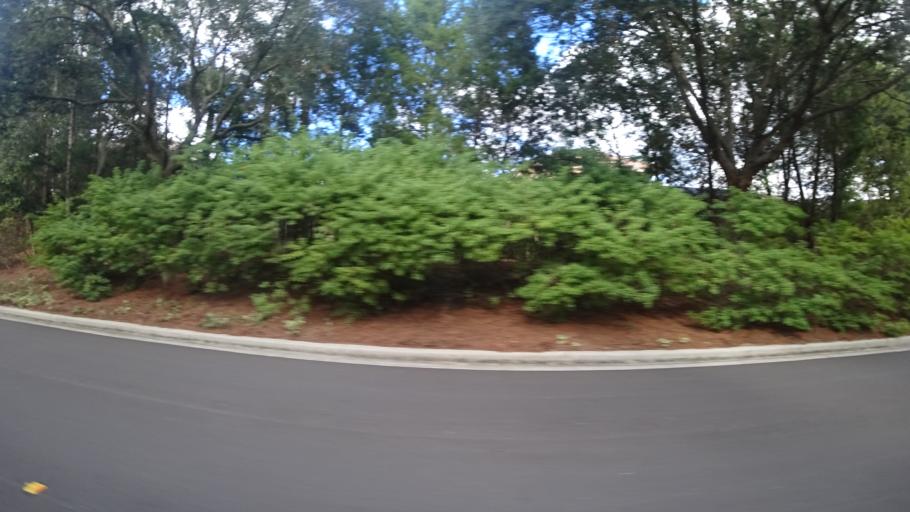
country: US
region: Florida
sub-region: Sarasota County
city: The Meadows
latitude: 27.4135
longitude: -82.4070
